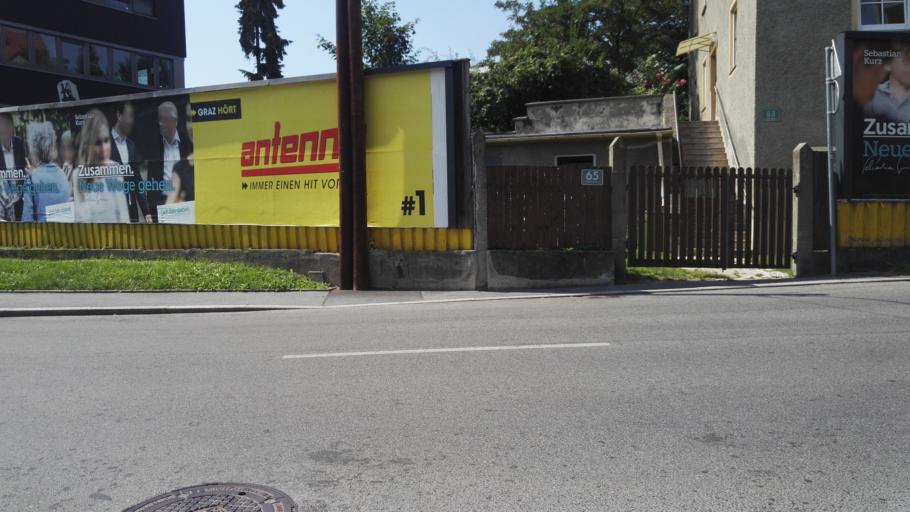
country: AT
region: Styria
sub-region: Graz Stadt
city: Goesting
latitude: 47.0791
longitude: 15.4197
